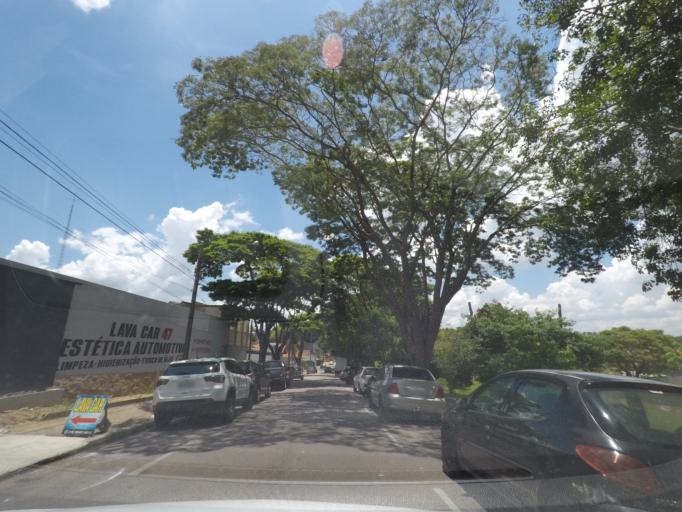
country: BR
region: Sao Paulo
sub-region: Vinhedo
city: Vinhedo
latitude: -23.0264
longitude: -46.9764
